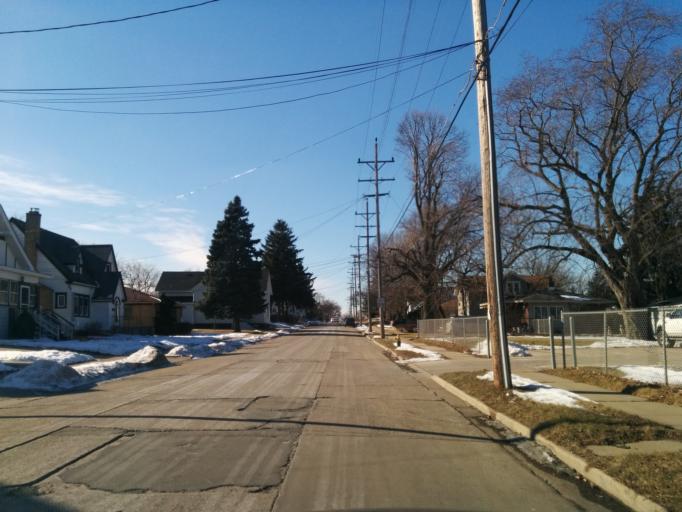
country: US
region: Wisconsin
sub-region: Racine County
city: Racine
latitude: 42.7369
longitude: -87.8081
